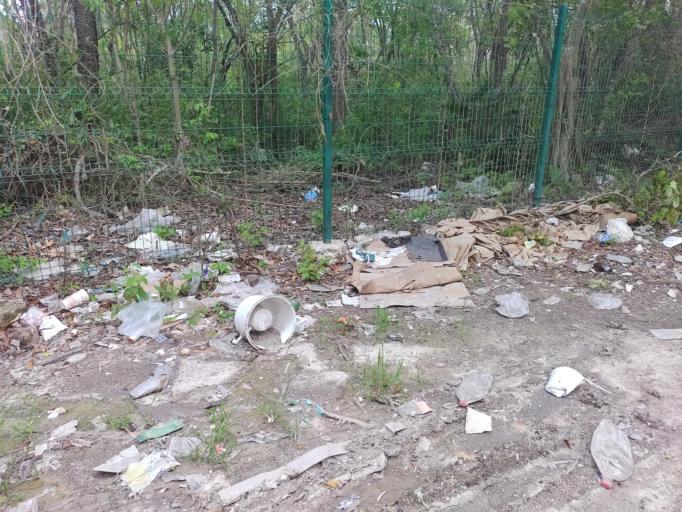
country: MX
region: Quintana Roo
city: Tulum
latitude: 20.2060
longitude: -87.4703
